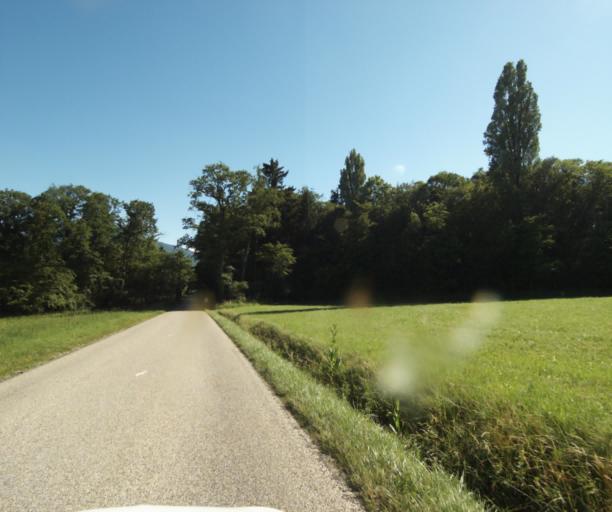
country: FR
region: Rhone-Alpes
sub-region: Departement de la Haute-Savoie
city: Ballaison
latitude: 46.2897
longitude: 6.3480
